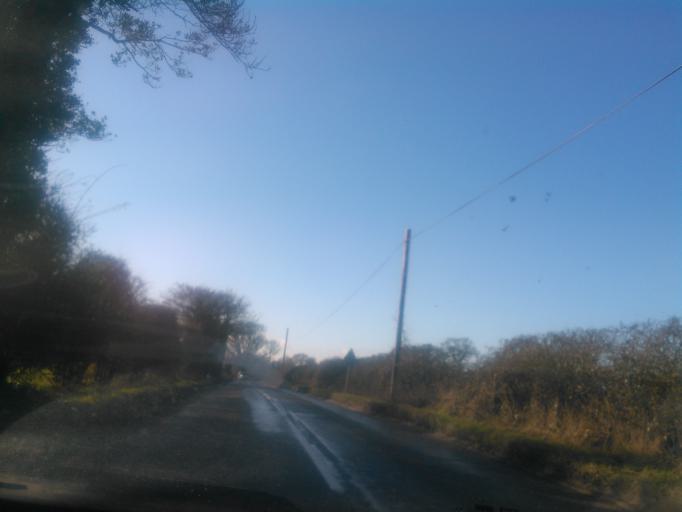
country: GB
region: England
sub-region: Shropshire
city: Wem
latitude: 52.8676
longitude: -2.6955
